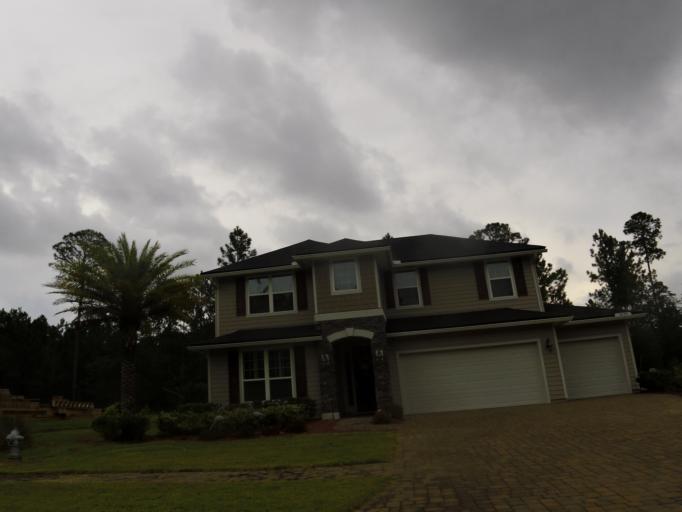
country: US
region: Florida
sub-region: Clay County
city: Middleburg
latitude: 30.1135
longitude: -81.8612
